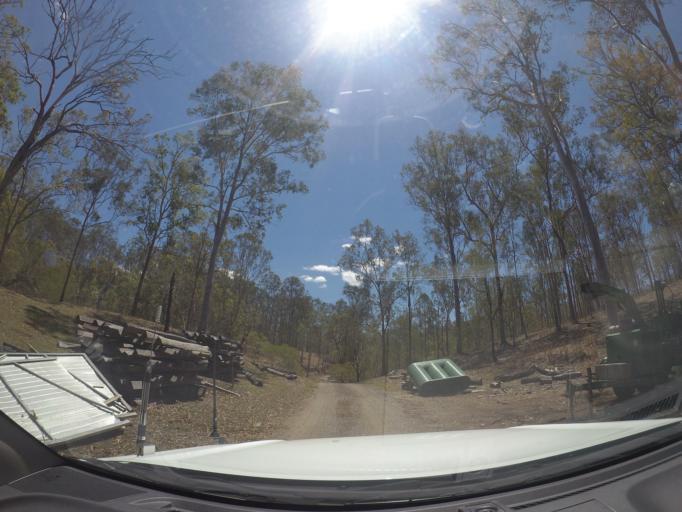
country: AU
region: Queensland
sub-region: Ipswich
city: Deebing Heights
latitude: -27.7687
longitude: 152.8117
